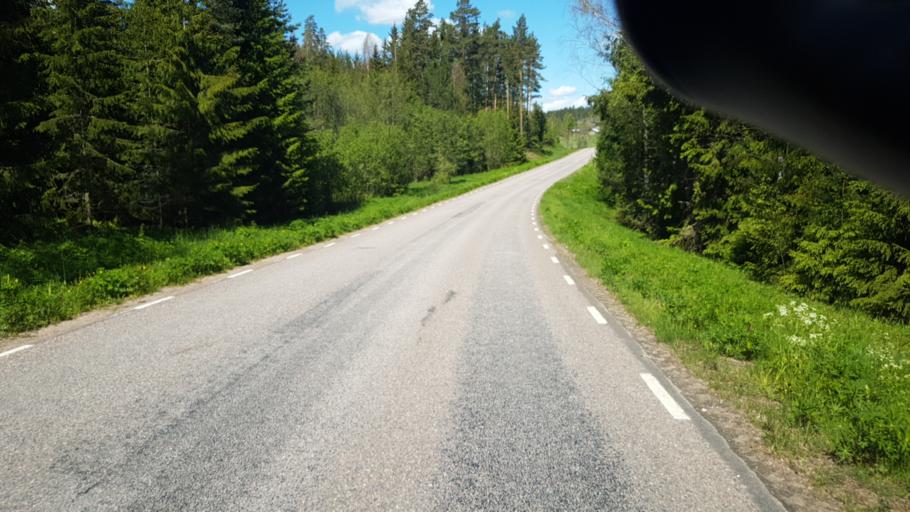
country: SE
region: Vaermland
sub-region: Arvika Kommun
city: Arvika
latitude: 59.6296
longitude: 12.7999
